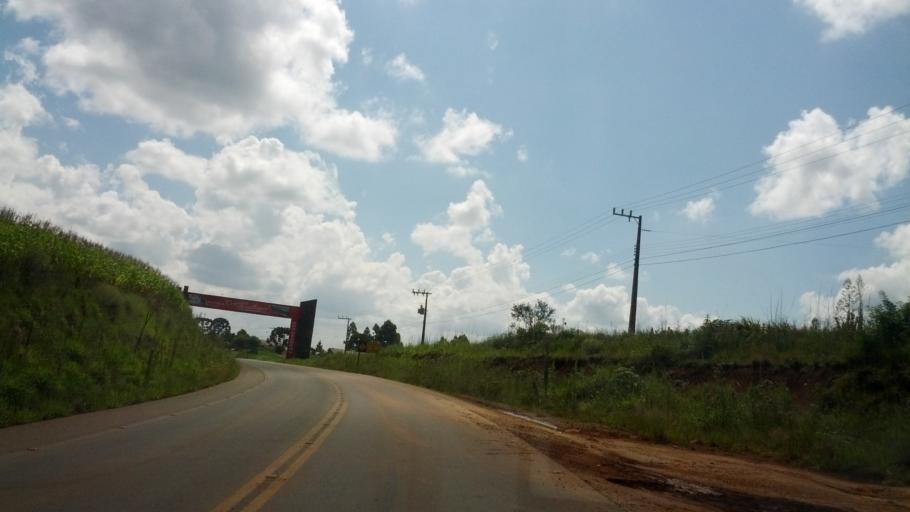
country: BR
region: Rio Grande do Sul
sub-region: Vacaria
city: Estrela
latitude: -27.7974
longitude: -50.8639
